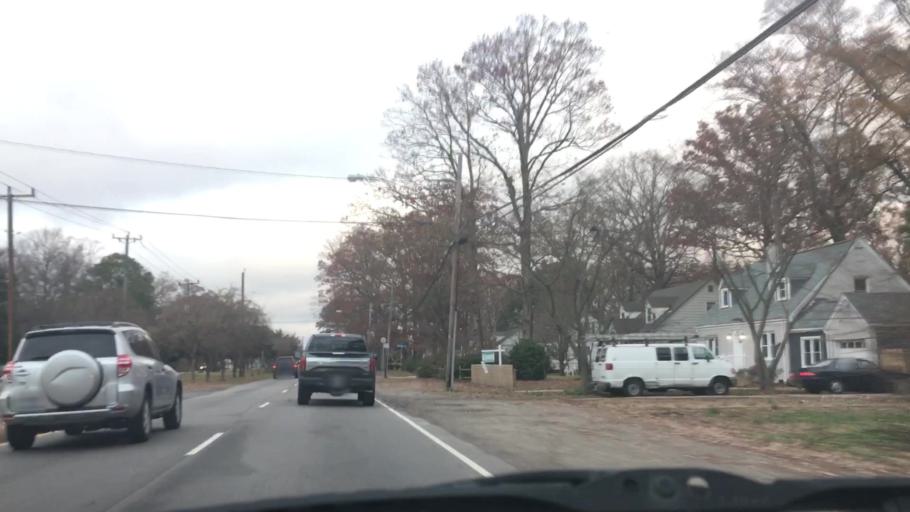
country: US
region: Virginia
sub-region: City of Norfolk
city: Norfolk
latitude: 36.9258
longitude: -76.2431
